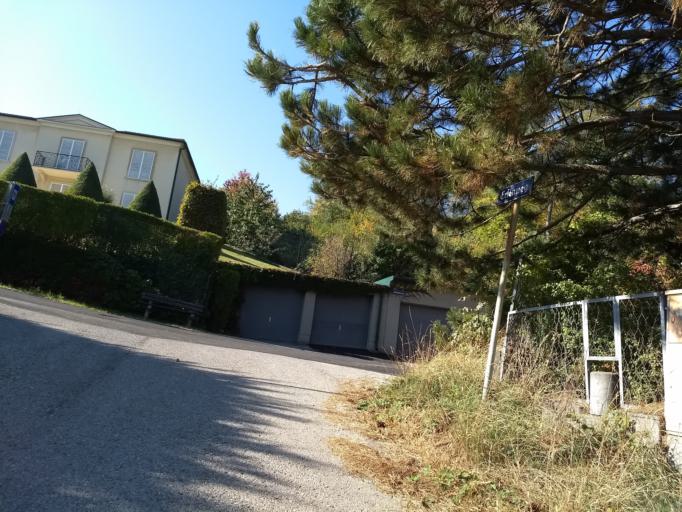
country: AT
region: Lower Austria
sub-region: Politischer Bezirk Modling
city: Giesshubl
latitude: 48.1046
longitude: 16.2397
